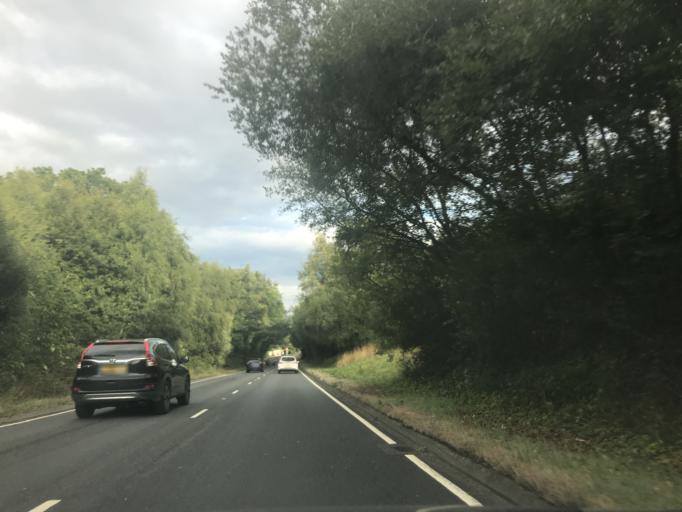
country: GB
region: England
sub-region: Surrey
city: Bagshot
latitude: 51.3798
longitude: -0.7106
